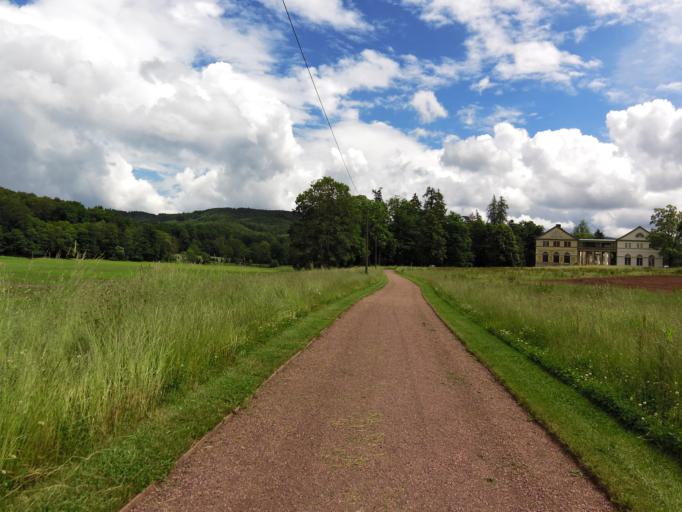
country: DE
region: Thuringia
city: Wolfsburg-Unkeroda
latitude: 50.9203
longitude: 10.3003
